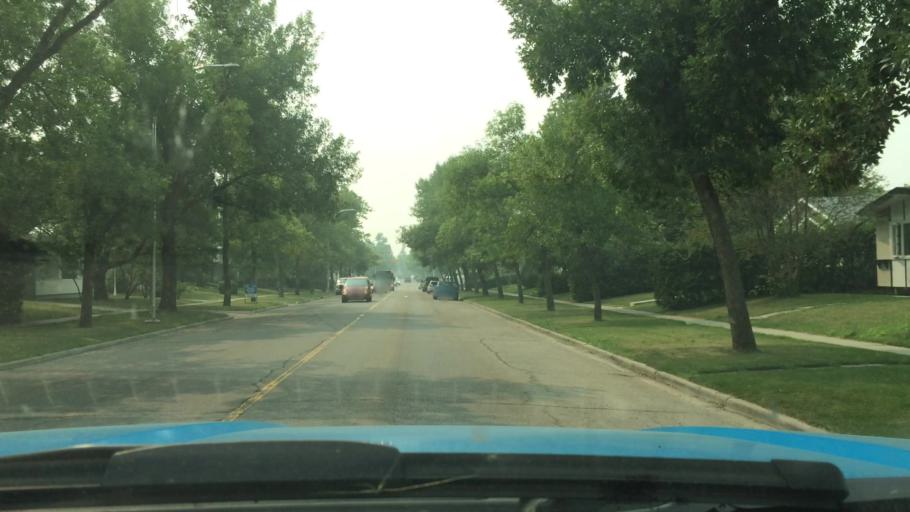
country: CA
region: Alberta
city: Calgary
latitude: 51.0946
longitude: -114.1272
